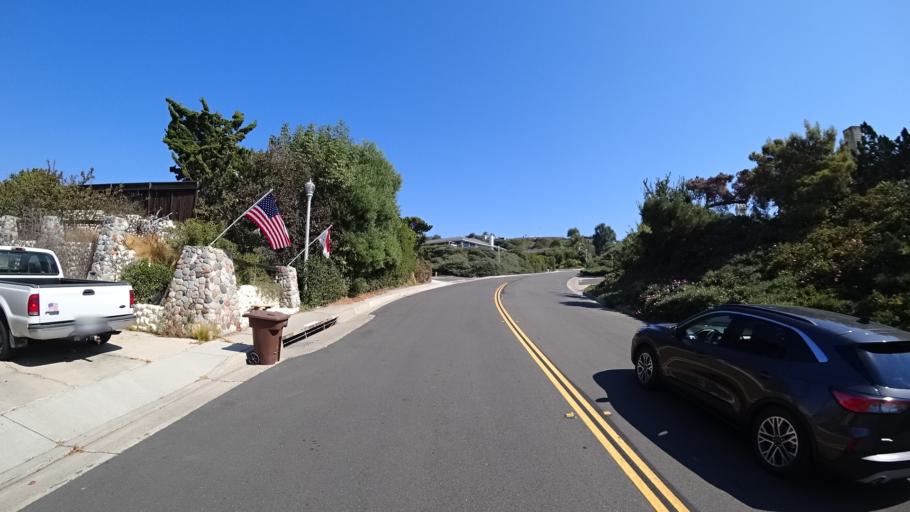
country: US
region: California
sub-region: Orange County
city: San Clemente
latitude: 33.4348
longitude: -117.6086
